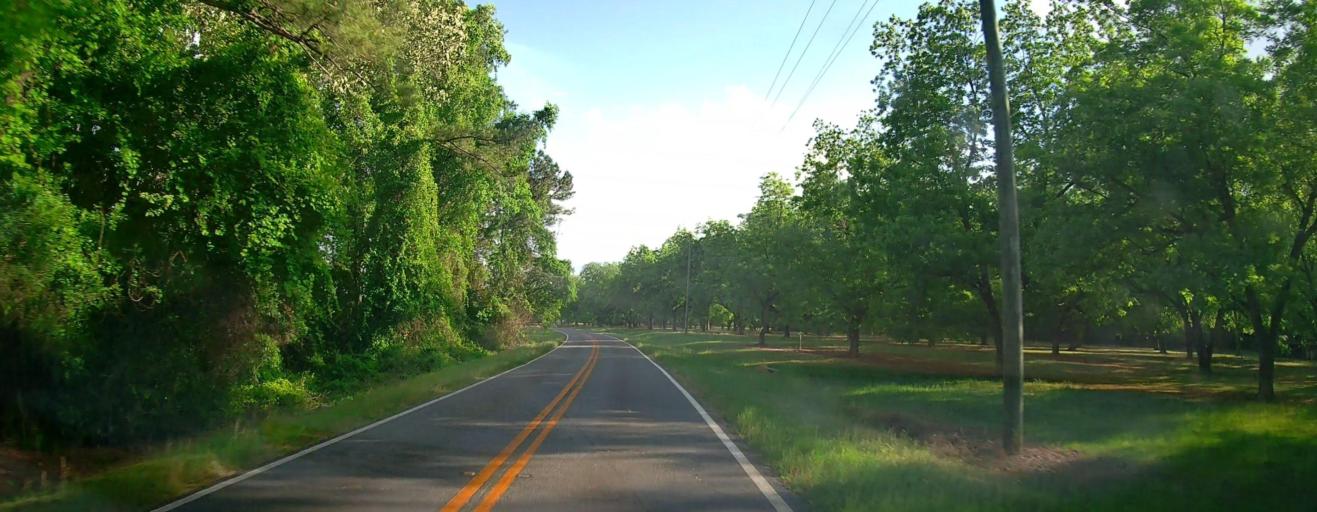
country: US
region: Georgia
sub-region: Peach County
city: Byron
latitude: 32.6699
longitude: -83.8017
